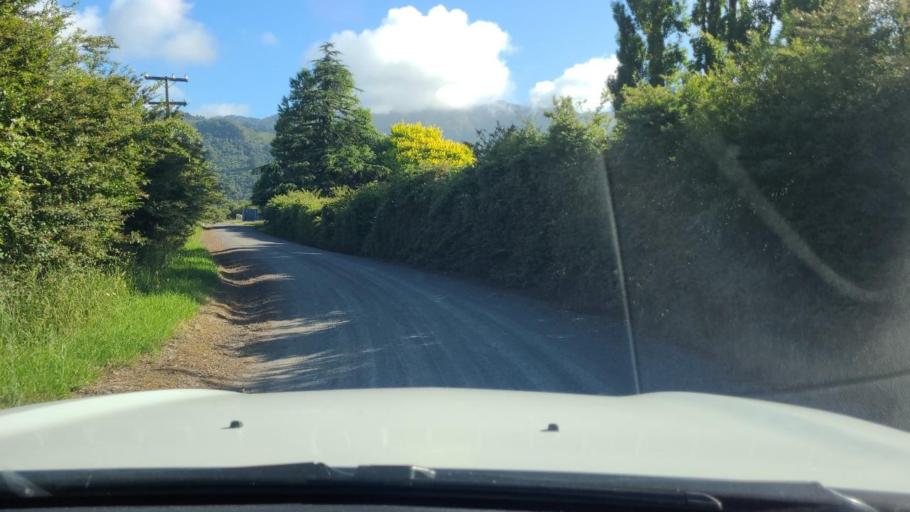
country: NZ
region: Bay of Plenty
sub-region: Western Bay of Plenty District
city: Katikati
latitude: -37.5753
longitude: 175.7619
